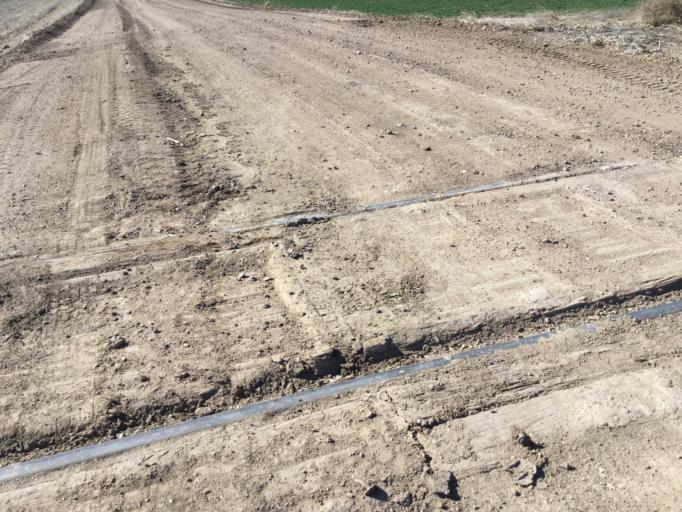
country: US
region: Kansas
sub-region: Grant County
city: Ulysses
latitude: 37.5622
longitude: -101.5263
